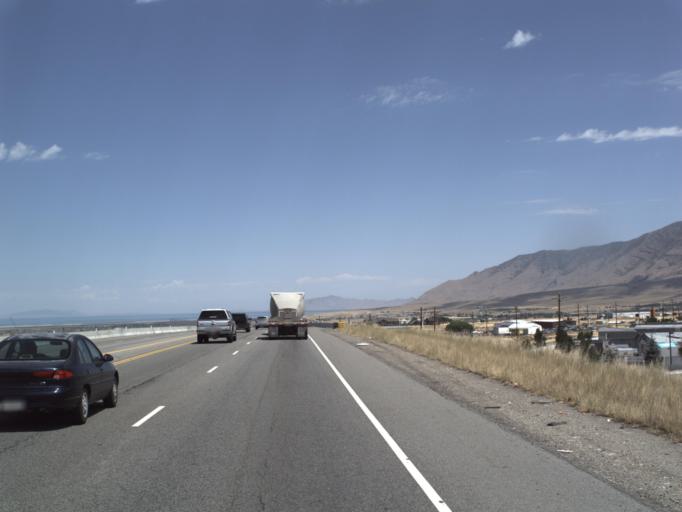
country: US
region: Utah
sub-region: Tooele County
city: Tooele
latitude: 40.5575
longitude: -112.2970
